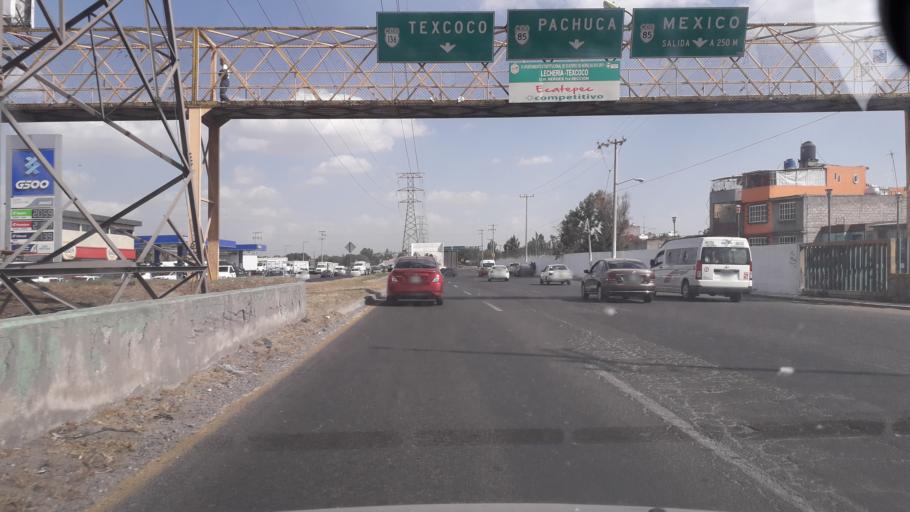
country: MX
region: Mexico
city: Ecatepec
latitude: 19.6142
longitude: -99.0373
